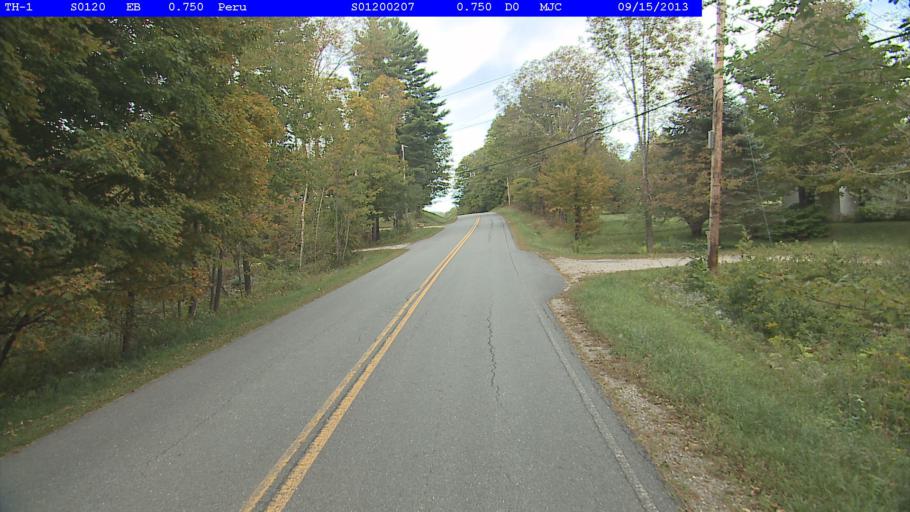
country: US
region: Vermont
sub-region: Bennington County
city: Manchester Center
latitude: 43.2367
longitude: -72.8984
